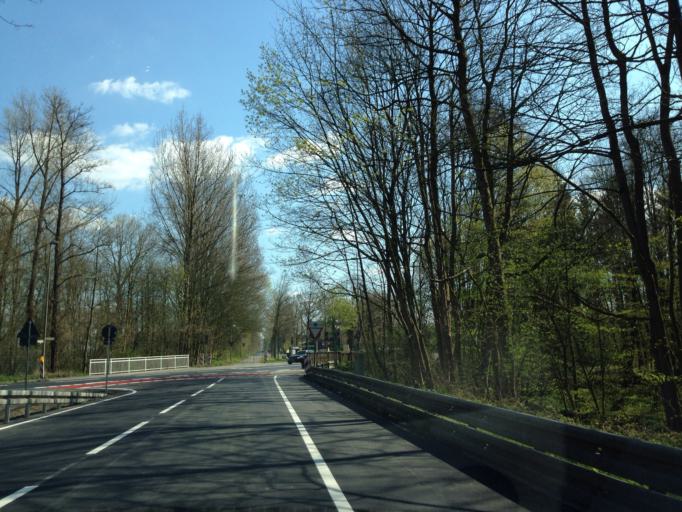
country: DE
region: North Rhine-Westphalia
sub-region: Regierungsbezirk Munster
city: Muenster
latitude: 52.0031
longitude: 7.6143
